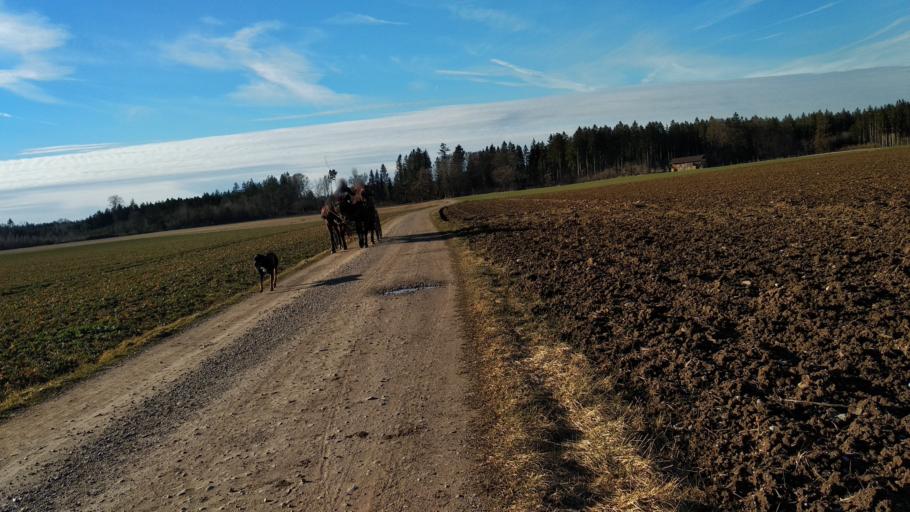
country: DE
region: Bavaria
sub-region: Upper Bavaria
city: Aying
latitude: 47.9810
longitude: 11.7703
